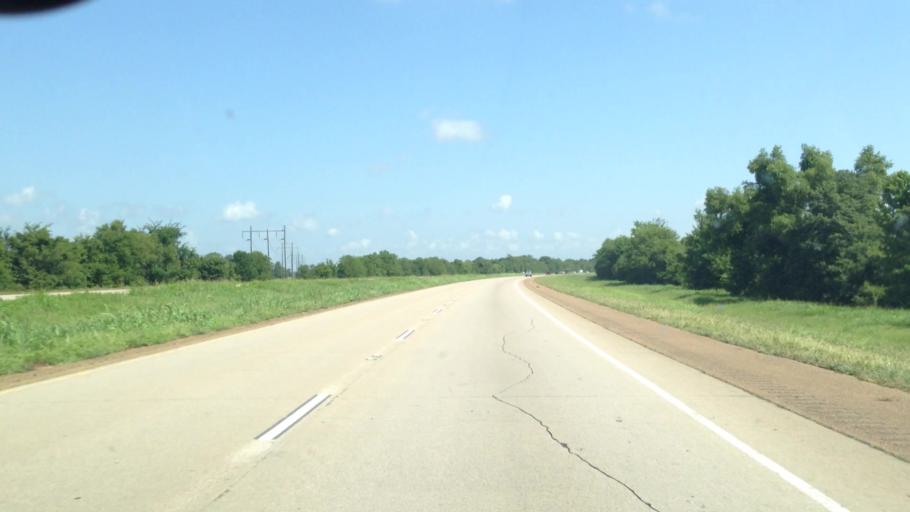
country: US
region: Louisiana
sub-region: Rapides Parish
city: Woodworth
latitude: 31.1882
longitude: -92.4724
